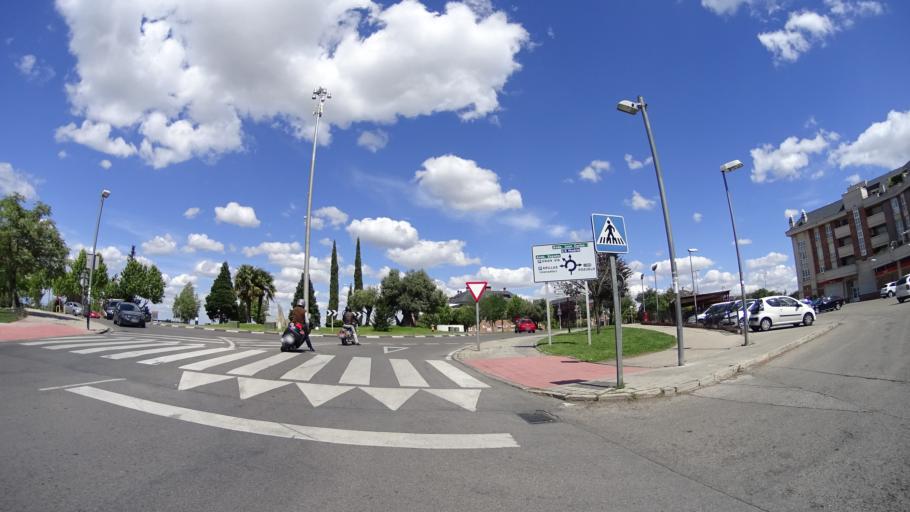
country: ES
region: Madrid
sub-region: Provincia de Madrid
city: Majadahonda
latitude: 40.4610
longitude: -3.8663
